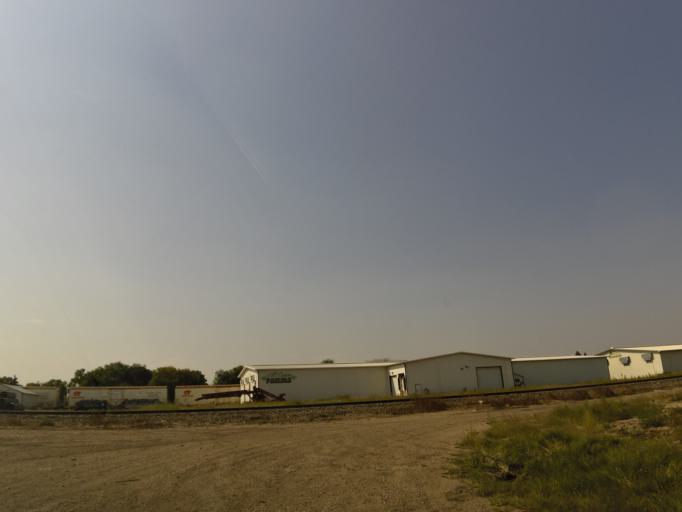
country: US
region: North Dakota
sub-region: Walsh County
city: Grafton
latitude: 48.4145
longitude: -97.4063
